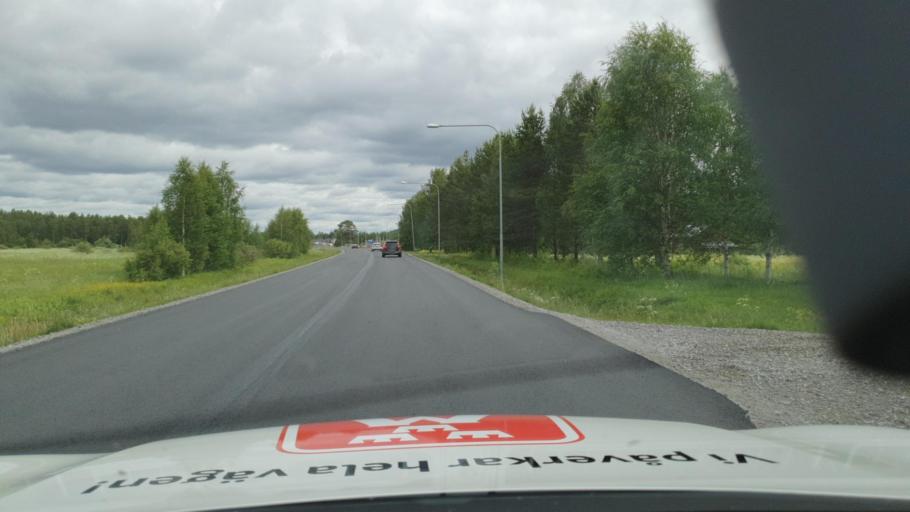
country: SE
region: Vaesterbotten
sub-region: Asele Kommun
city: Asele
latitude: 64.1635
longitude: 17.3274
